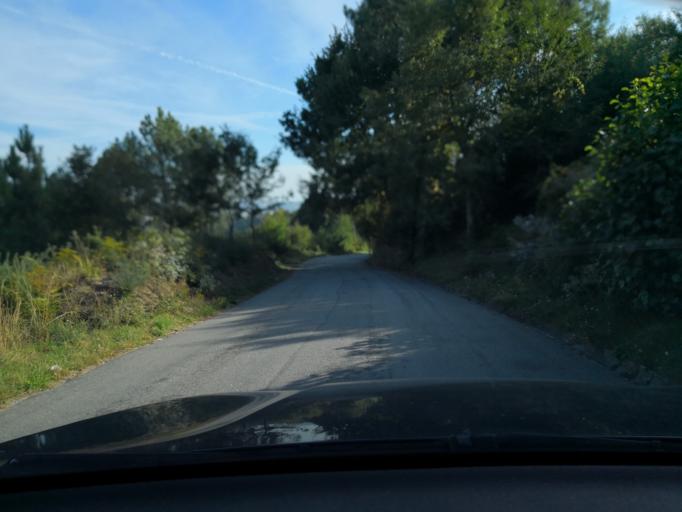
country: PT
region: Vila Real
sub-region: Vila Real
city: Vila Real
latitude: 41.3360
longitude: -7.7428
